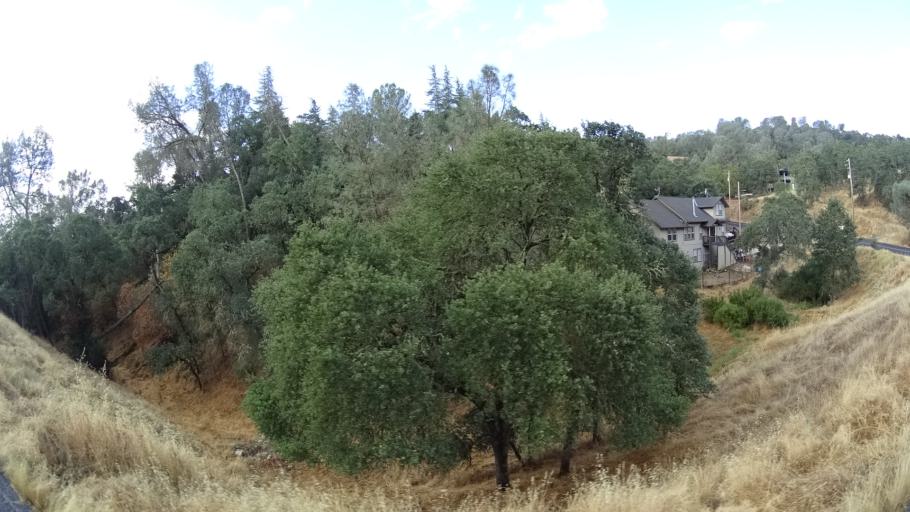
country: US
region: California
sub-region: Calaveras County
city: Copperopolis
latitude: 37.9151
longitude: -120.6061
